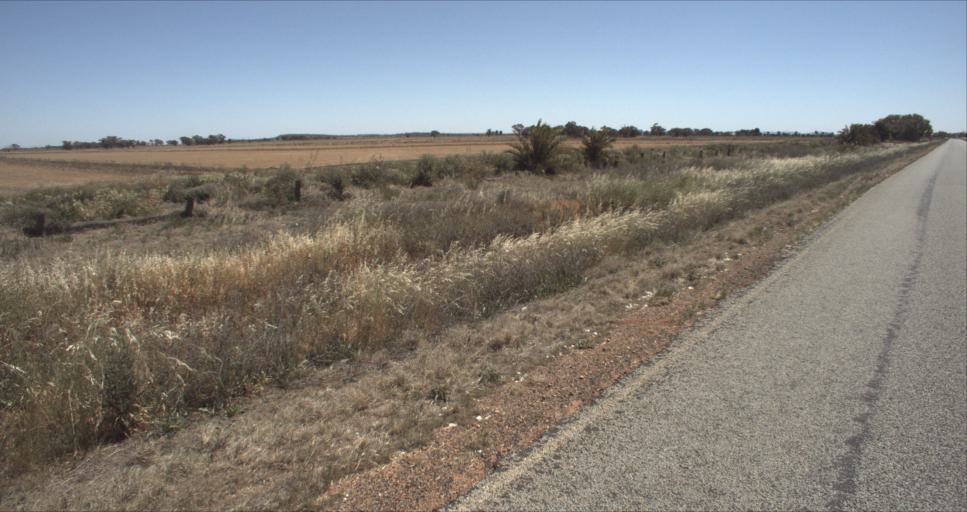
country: AU
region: New South Wales
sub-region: Leeton
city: Leeton
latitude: -34.4514
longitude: 146.2959
